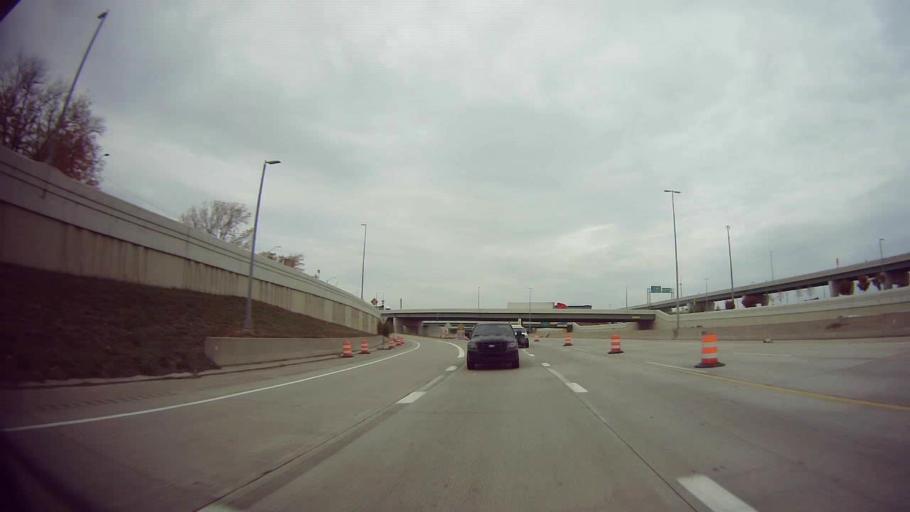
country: US
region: Michigan
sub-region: Wayne County
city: Detroit
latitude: 42.3189
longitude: -83.0827
